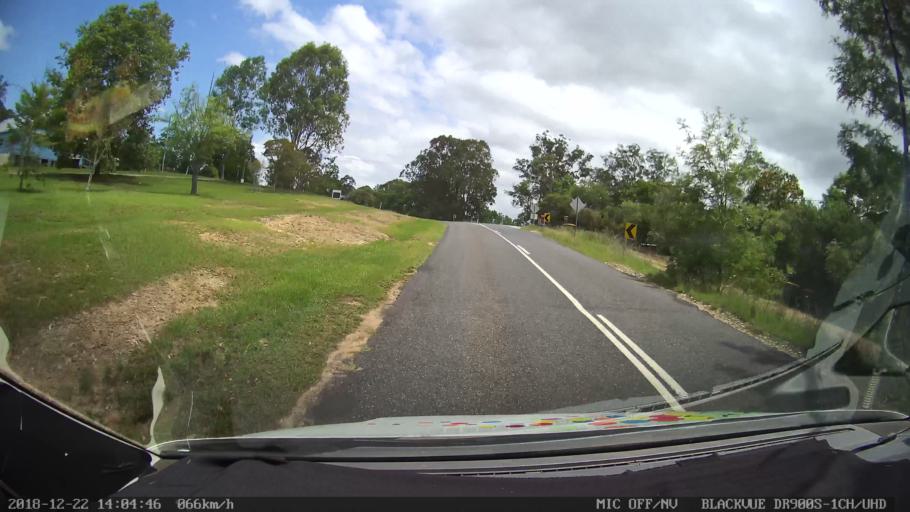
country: AU
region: New South Wales
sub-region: Clarence Valley
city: Coutts Crossing
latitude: -29.9379
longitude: 152.7267
